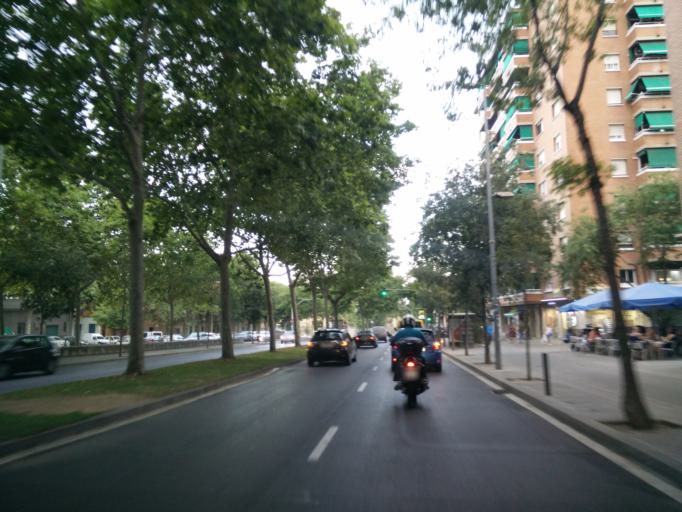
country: ES
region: Catalonia
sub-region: Provincia de Barcelona
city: Badalona
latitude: 41.4498
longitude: 2.2340
